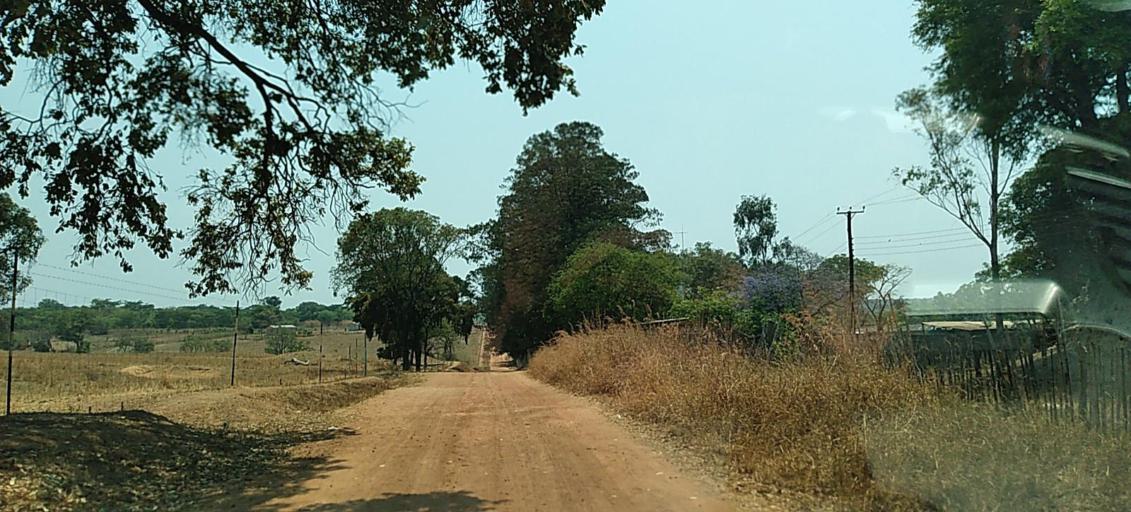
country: ZM
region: Copperbelt
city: Chambishi
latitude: -12.6238
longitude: 27.9426
